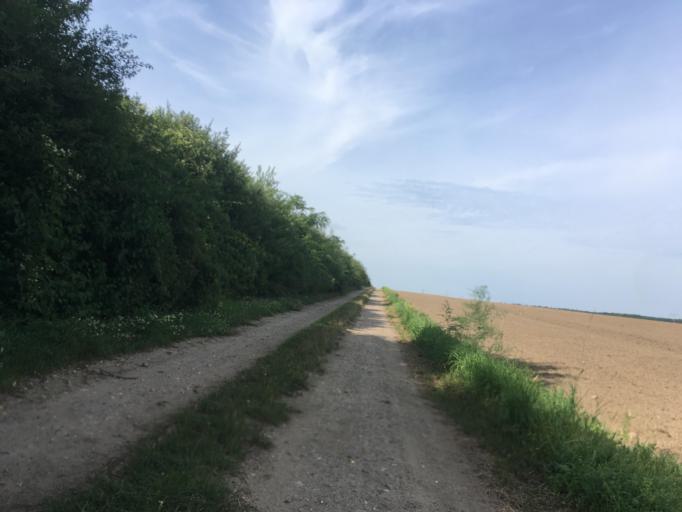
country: DE
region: Brandenburg
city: Melchow
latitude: 52.7169
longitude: 13.7244
